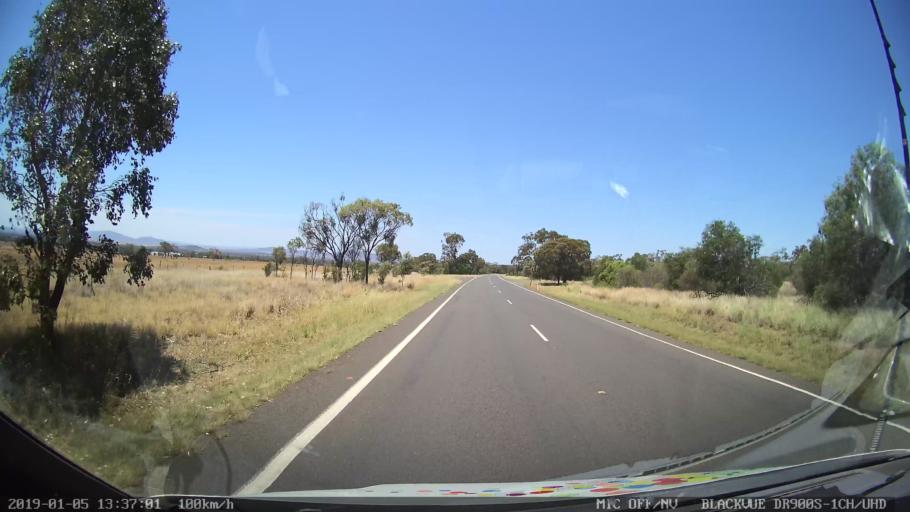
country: AU
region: New South Wales
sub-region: Gunnedah
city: Gunnedah
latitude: -30.9823
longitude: 150.1743
